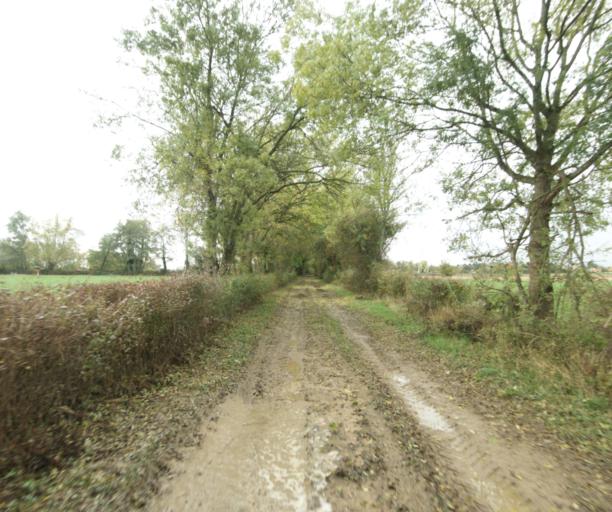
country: FR
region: Rhone-Alpes
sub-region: Departement de l'Ain
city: Pont-de-Vaux
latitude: 46.4786
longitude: 4.9042
